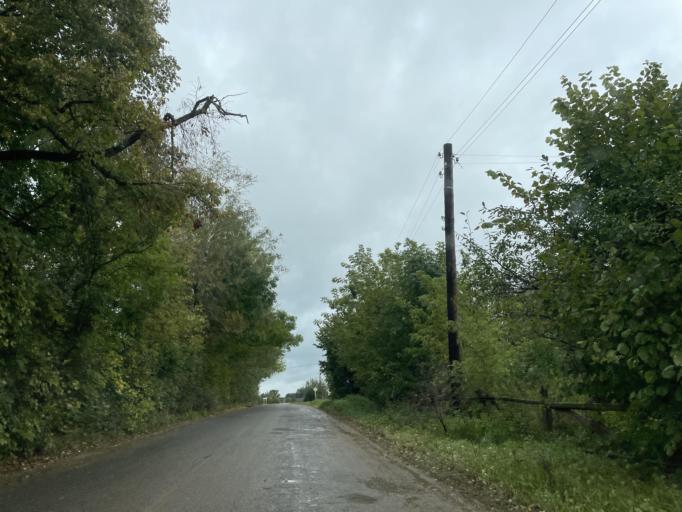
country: BY
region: Minsk
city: Snow
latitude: 53.1993
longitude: 26.2426
